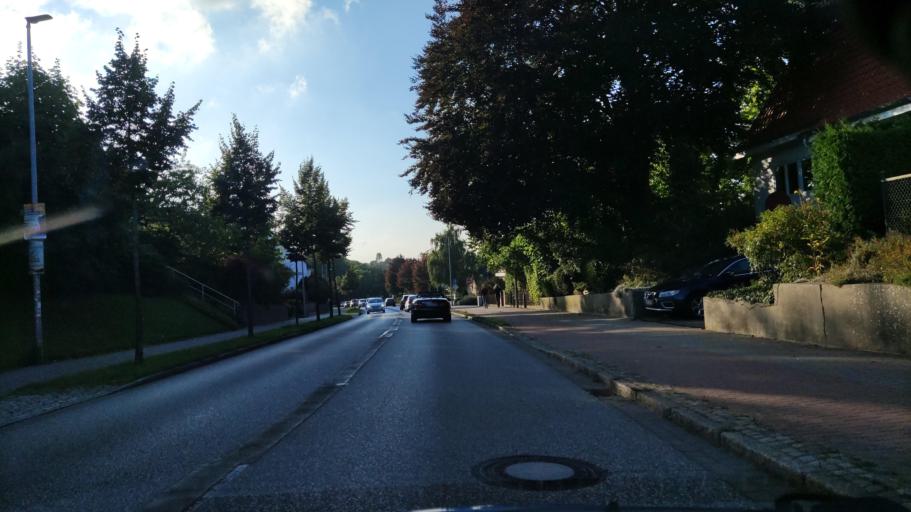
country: DE
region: Schleswig-Holstein
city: Ploen
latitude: 54.1585
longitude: 10.4367
